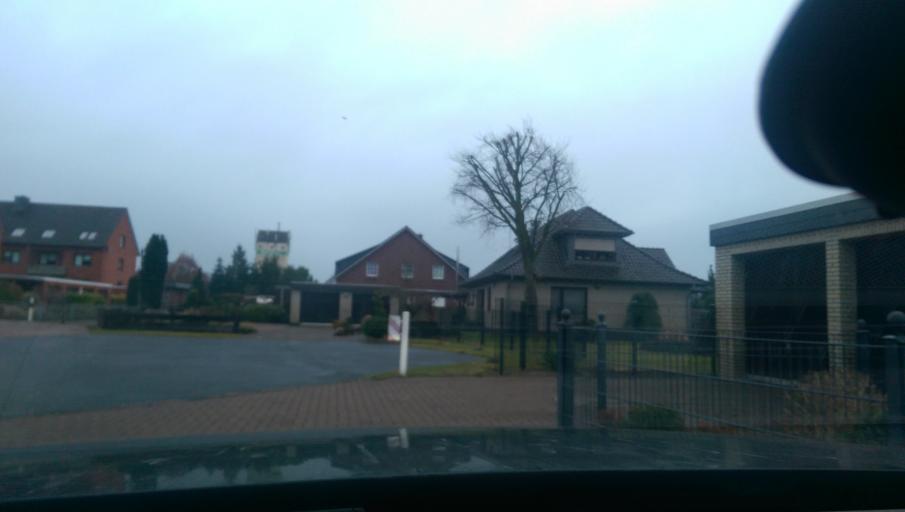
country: DE
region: Lower Saxony
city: Dorverden
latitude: 52.8486
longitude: 9.2312
